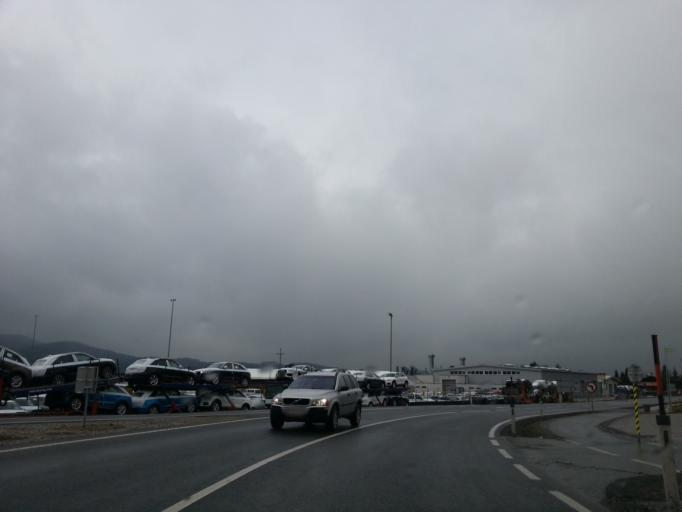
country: AT
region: Salzburg
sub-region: Politischer Bezirk Salzburg-Umgebung
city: Strasswalchen
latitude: 47.9862
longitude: 13.2518
